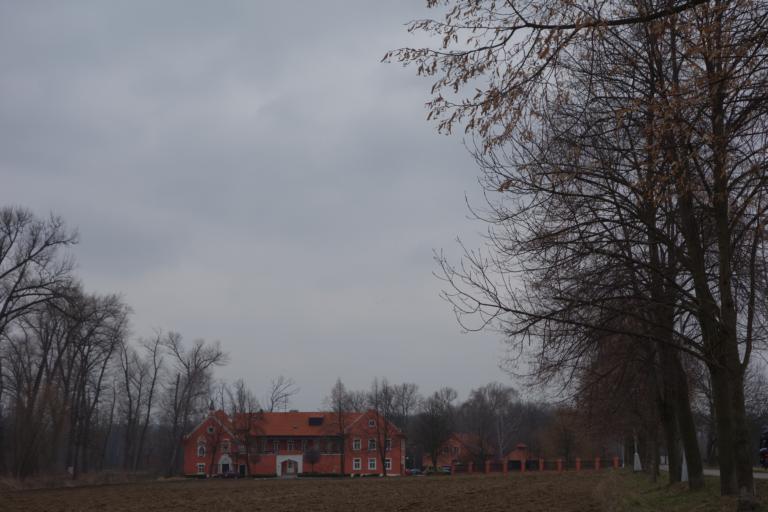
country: CZ
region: Central Bohemia
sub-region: Okres Melnik
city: Veltrusy
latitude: 50.2926
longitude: 14.3362
